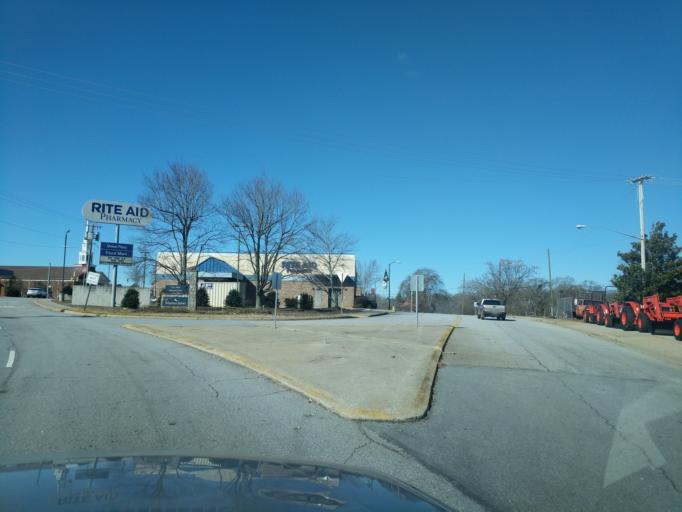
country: US
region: South Carolina
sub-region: Oconee County
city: Westminster
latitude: 34.6633
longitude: -83.0936
